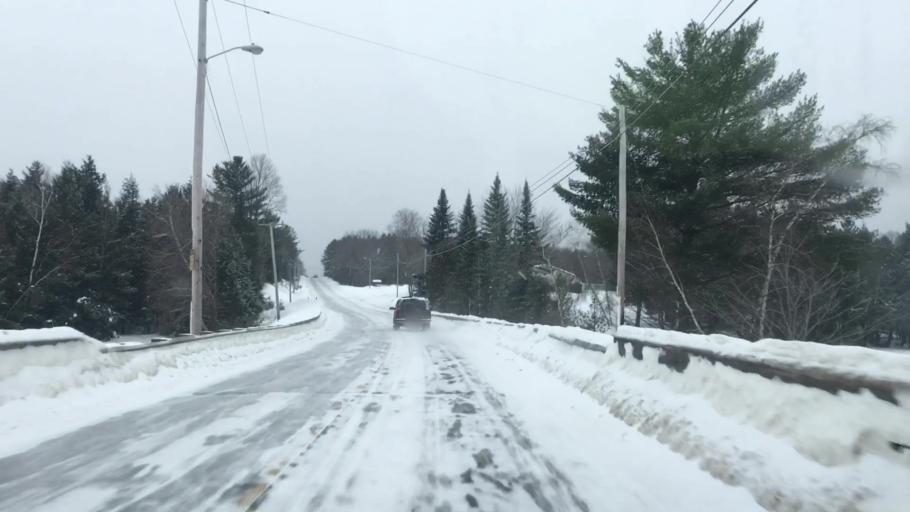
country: US
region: Maine
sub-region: Penobscot County
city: Medway
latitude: 45.5999
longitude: -68.4683
